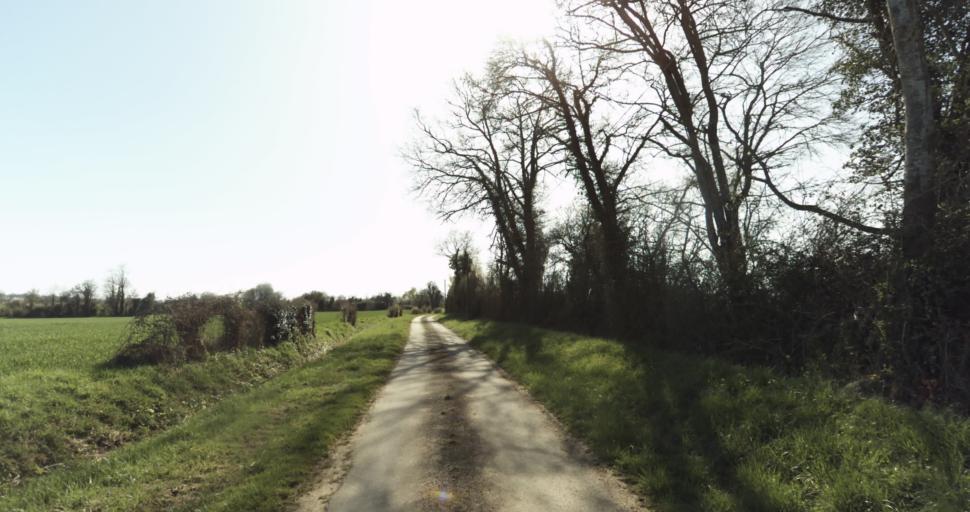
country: FR
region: Lower Normandy
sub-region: Departement de l'Orne
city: Trun
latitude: 48.9294
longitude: 0.0015
